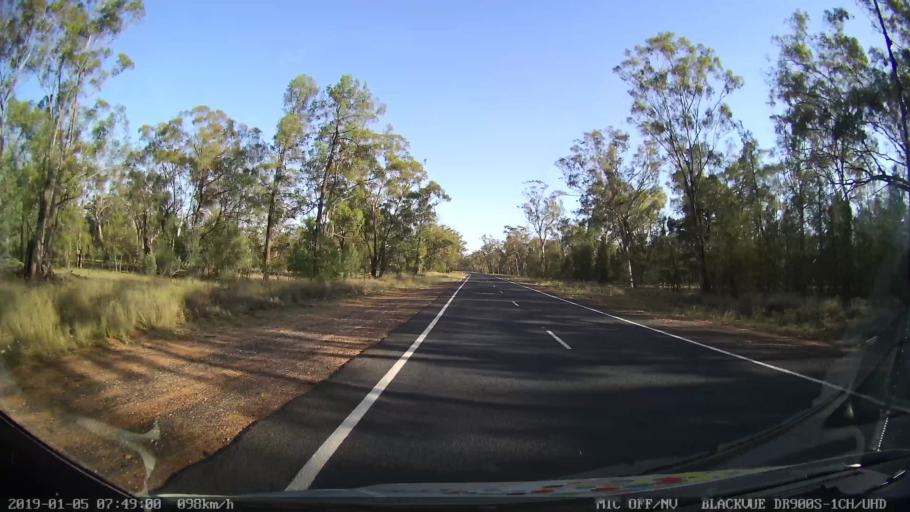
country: AU
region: New South Wales
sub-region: Gilgandra
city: Gilgandra
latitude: -31.8081
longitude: 148.6364
